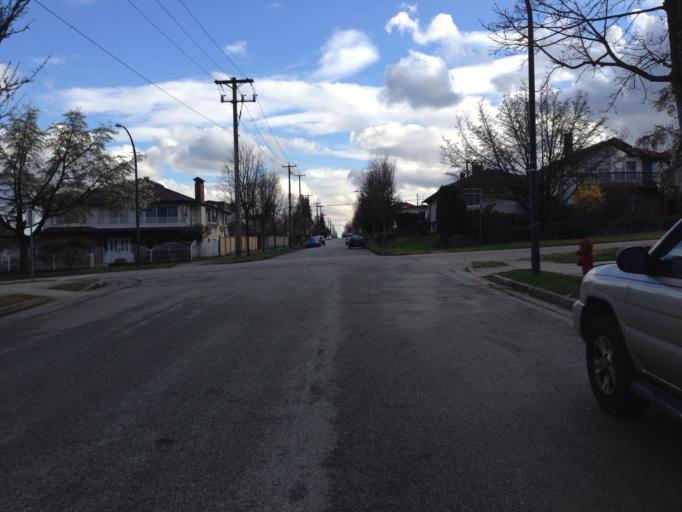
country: CA
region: British Columbia
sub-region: Fraser Valley Regional District
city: North Vancouver
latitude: 49.2736
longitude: -123.0389
